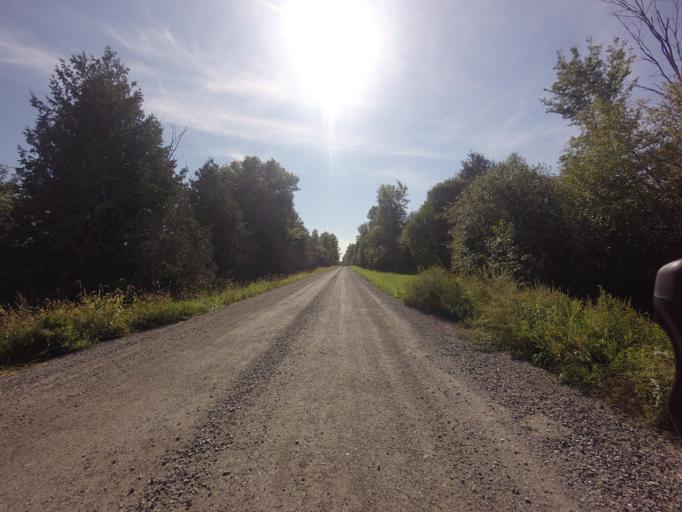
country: CA
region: Ontario
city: Perth
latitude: 44.9576
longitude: -76.3453
